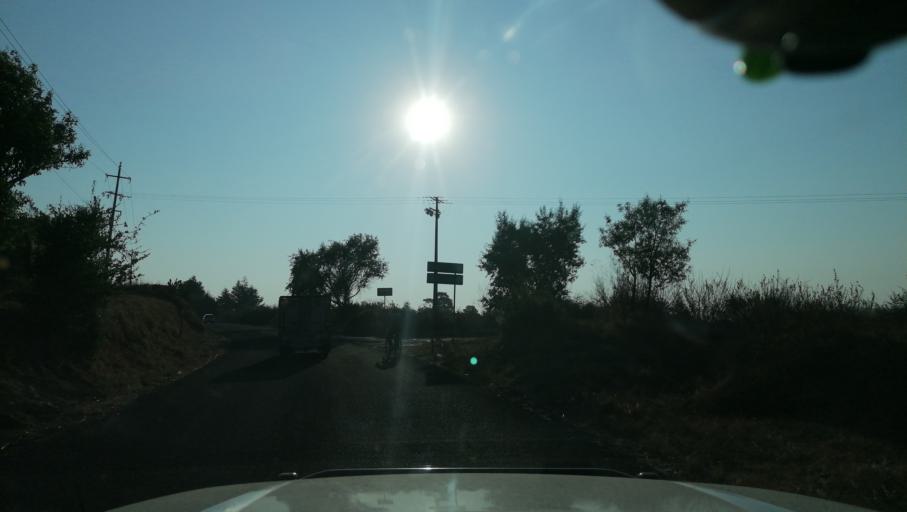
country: MX
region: Puebla
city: San Andres Calpan
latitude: 19.1050
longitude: -98.4401
